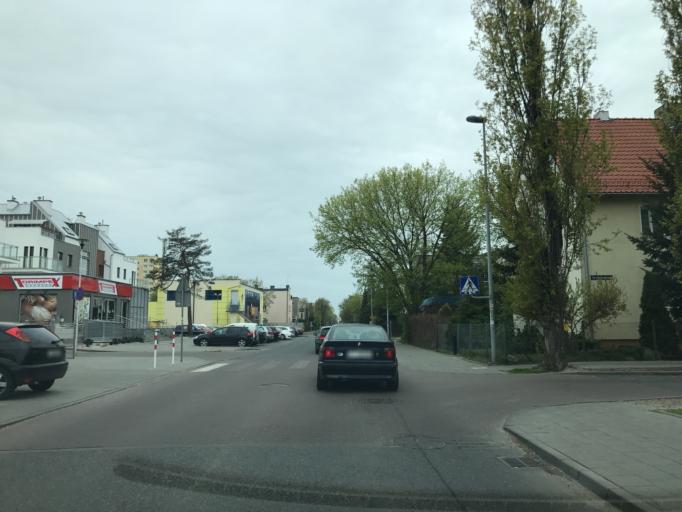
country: PL
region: Kujawsko-Pomorskie
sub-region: Torun
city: Torun
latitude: 53.0152
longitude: 18.5763
